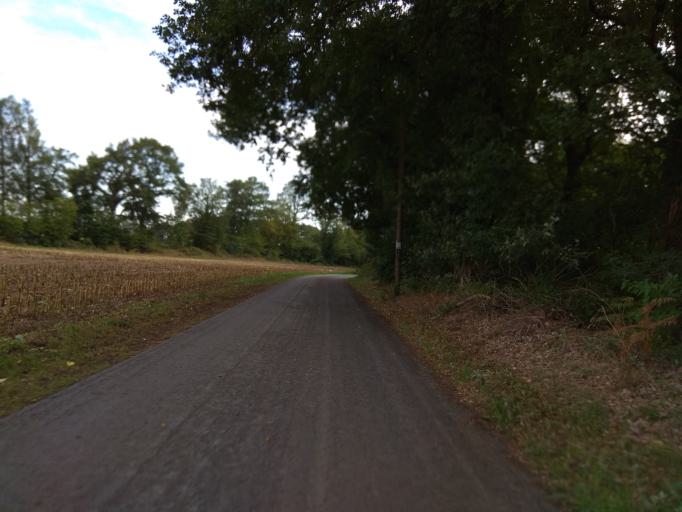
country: DE
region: North Rhine-Westphalia
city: Marl
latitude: 51.7069
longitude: 7.0609
